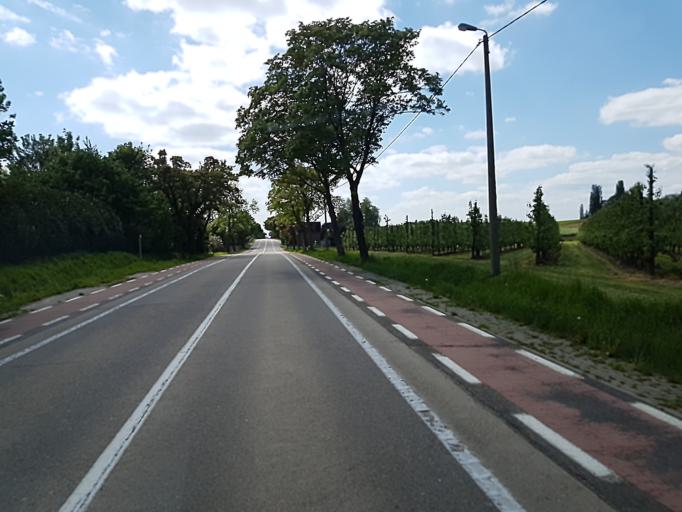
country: BE
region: Flanders
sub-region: Provincie Vlaams-Brabant
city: Glabbeek-Zuurbemde
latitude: 50.8815
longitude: 4.9648
